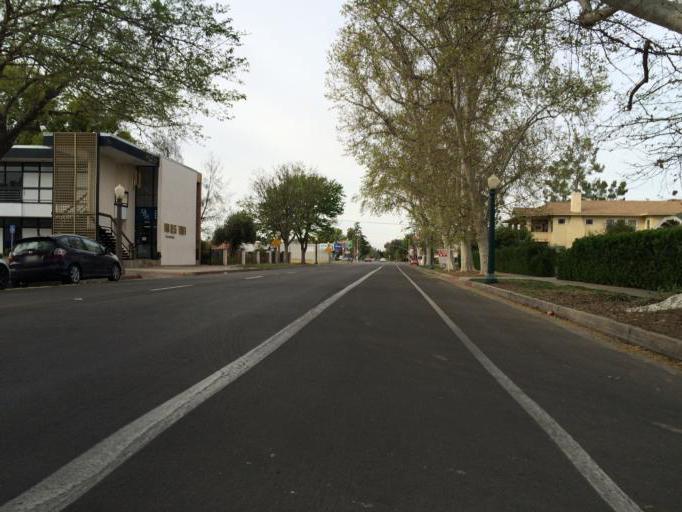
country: US
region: California
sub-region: Fresno County
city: Fresno
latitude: 36.7558
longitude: -119.7988
